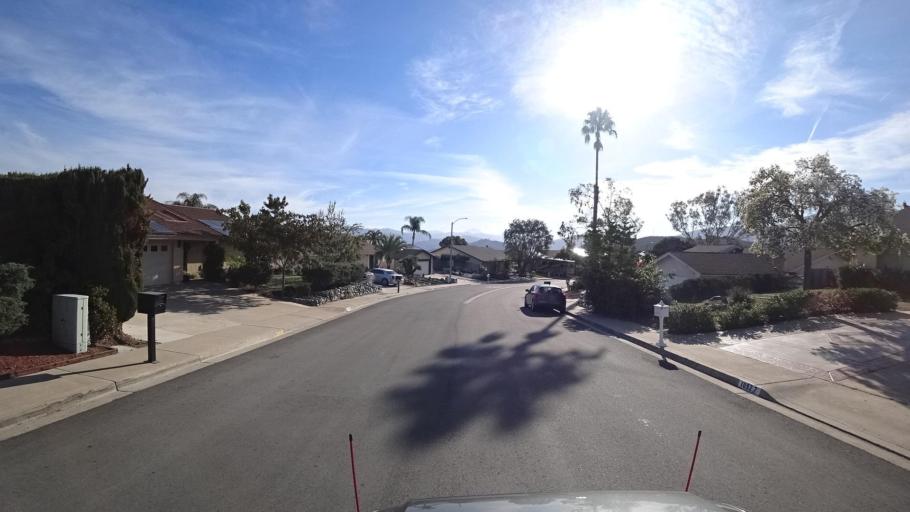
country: US
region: California
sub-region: San Diego County
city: Rancho San Diego
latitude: 32.7407
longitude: -116.9583
